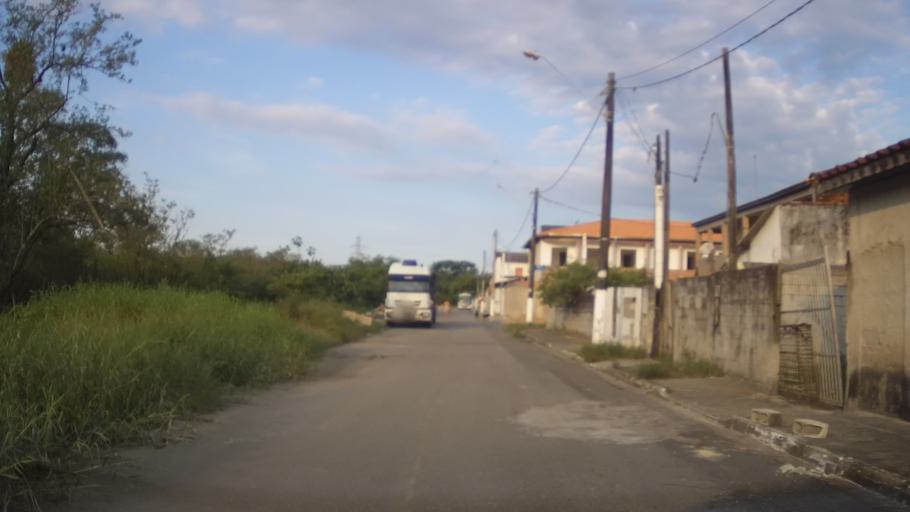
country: BR
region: Sao Paulo
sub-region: Praia Grande
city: Praia Grande
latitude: -23.9952
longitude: -46.4309
